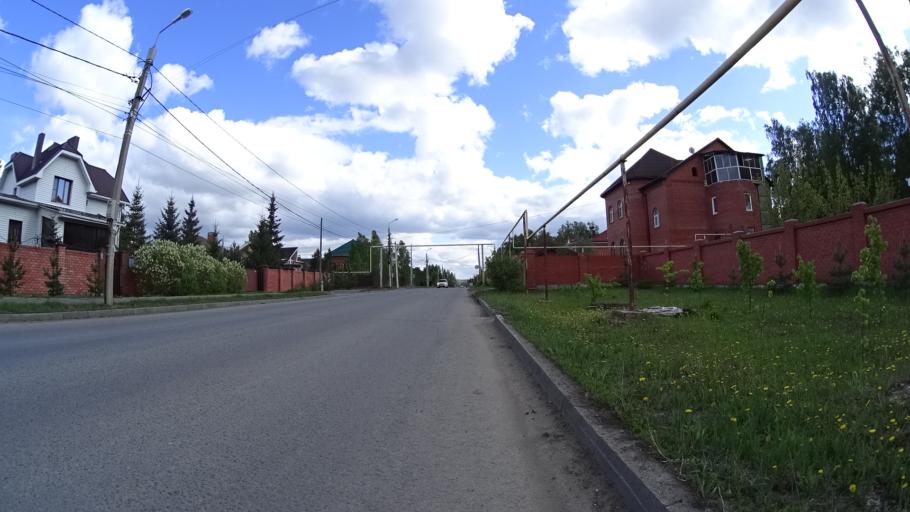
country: RU
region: Chelyabinsk
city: Sargazy
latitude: 55.1600
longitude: 61.2517
